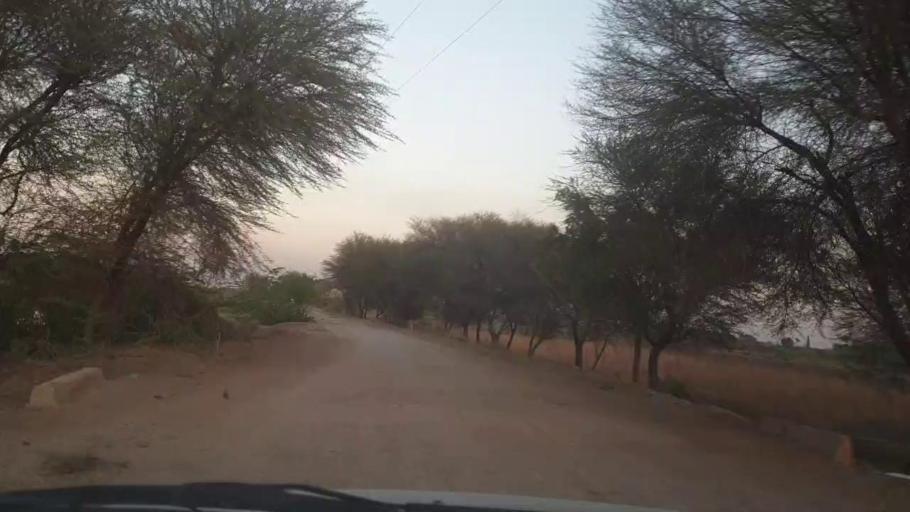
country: PK
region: Sindh
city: Mirpur Khas
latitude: 25.4971
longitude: 69.0400
